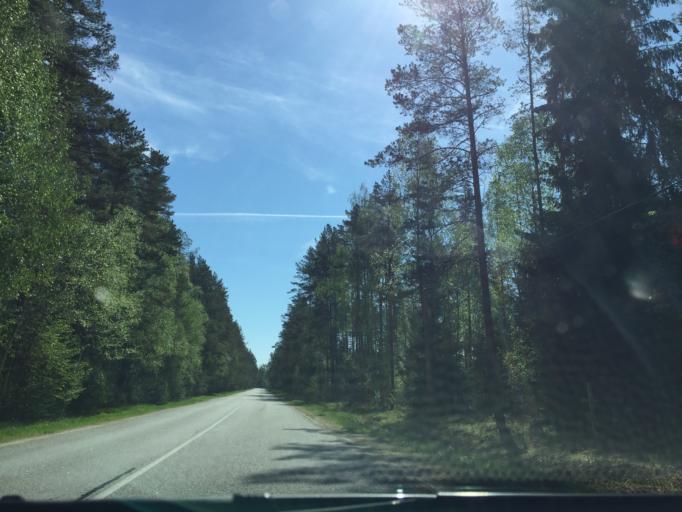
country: LV
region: Garkalne
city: Garkalne
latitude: 57.0154
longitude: 24.4449
